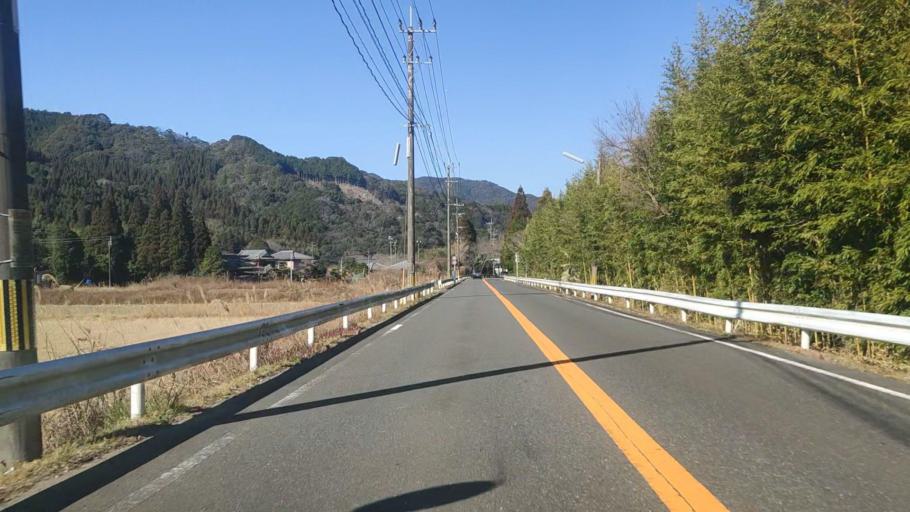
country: JP
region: Oita
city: Saiki
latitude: 32.9001
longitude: 131.9352
